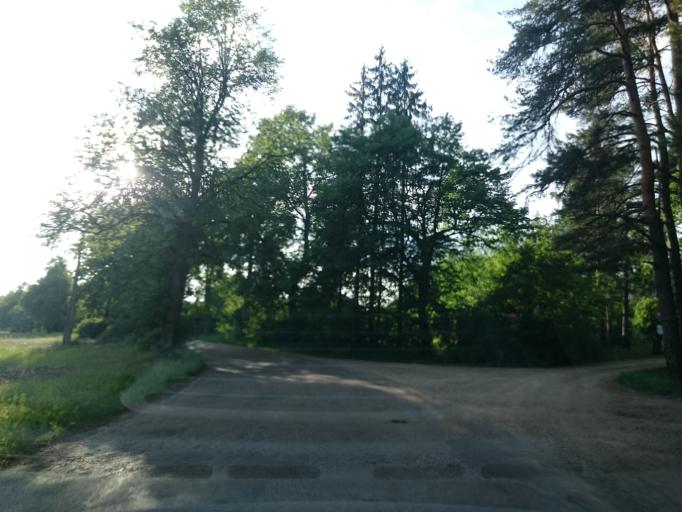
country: LV
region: Seja
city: Loja
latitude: 57.1225
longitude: 24.6467
